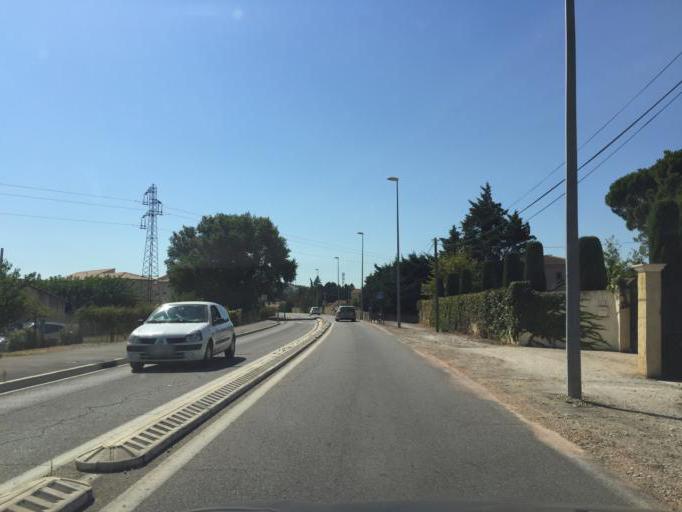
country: FR
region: Provence-Alpes-Cote d'Azur
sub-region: Departement du Vaucluse
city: Vedene
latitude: 43.9766
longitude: 4.9092
